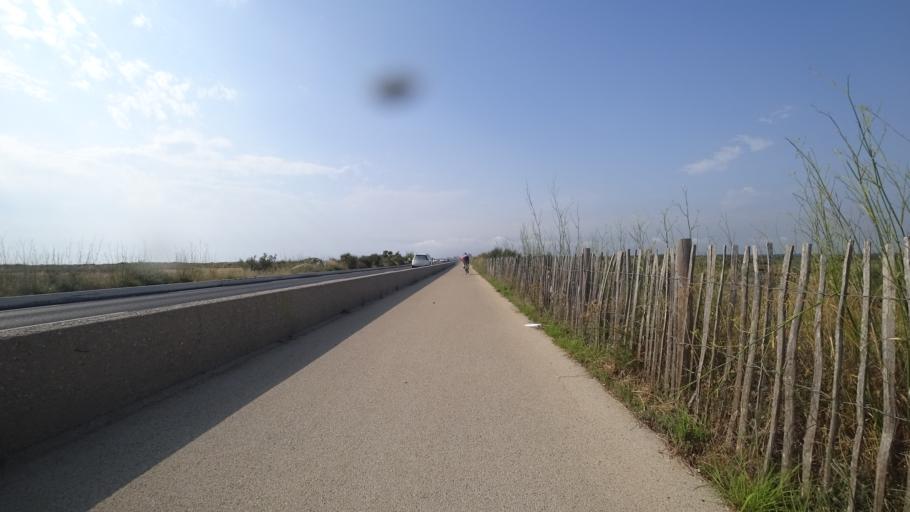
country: FR
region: Languedoc-Roussillon
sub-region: Departement des Pyrenees-Orientales
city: Saint-Cyprien-Plage
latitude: 42.6565
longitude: 3.0328
